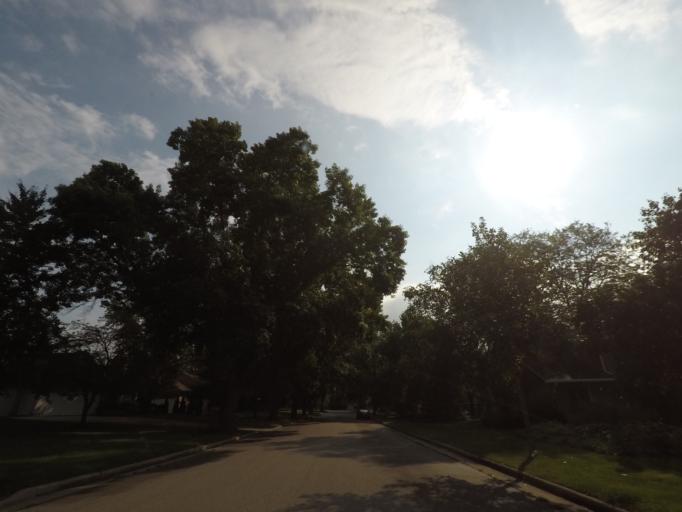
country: US
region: Wisconsin
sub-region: Dane County
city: Shorewood Hills
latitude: 43.0380
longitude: -89.4669
